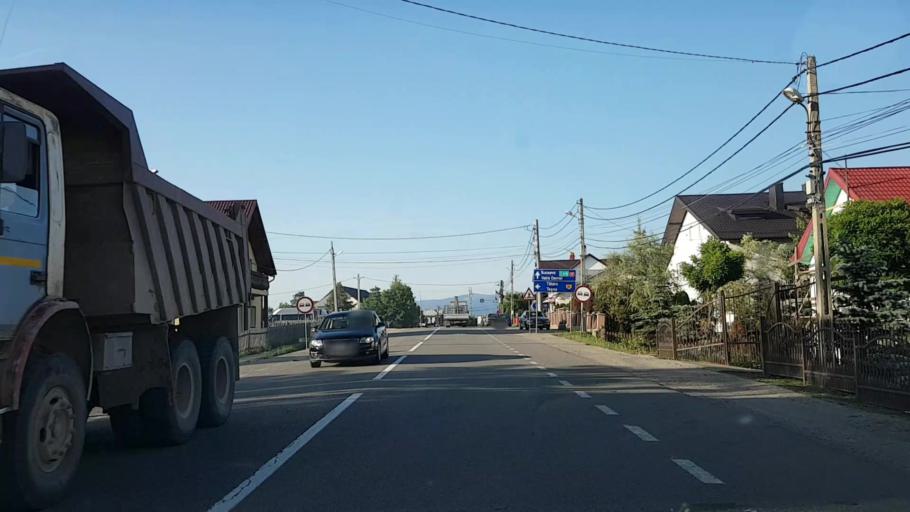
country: RO
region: Suceava
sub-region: Comuna Poiana Stampei
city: Poiana Stampei
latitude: 47.3225
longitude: 25.1386
